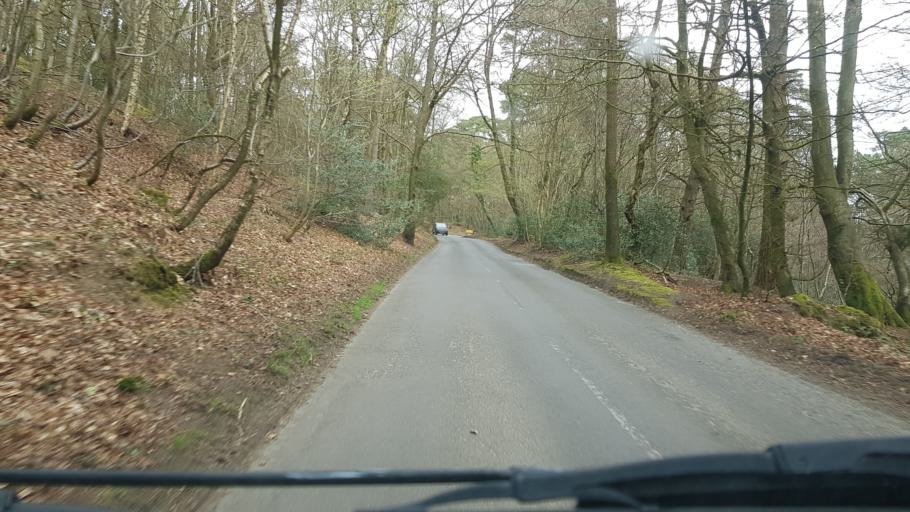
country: GB
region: England
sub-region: Surrey
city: Cranleigh
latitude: 51.1737
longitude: -0.4574
